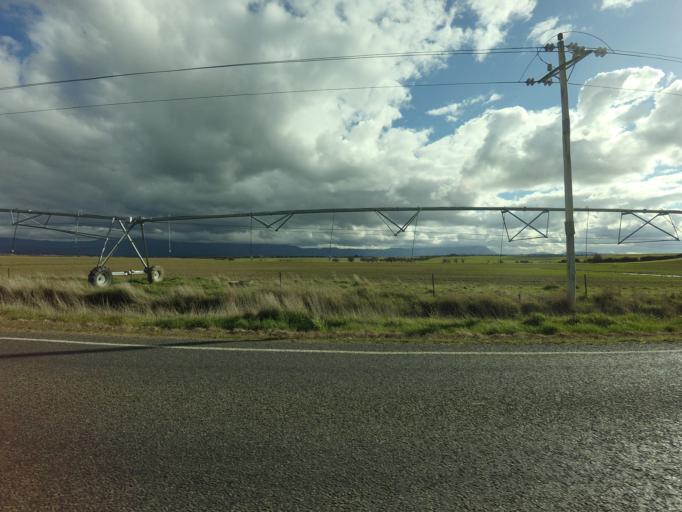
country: AU
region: Tasmania
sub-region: Northern Midlands
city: Longford
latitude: -41.7055
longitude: 147.0785
